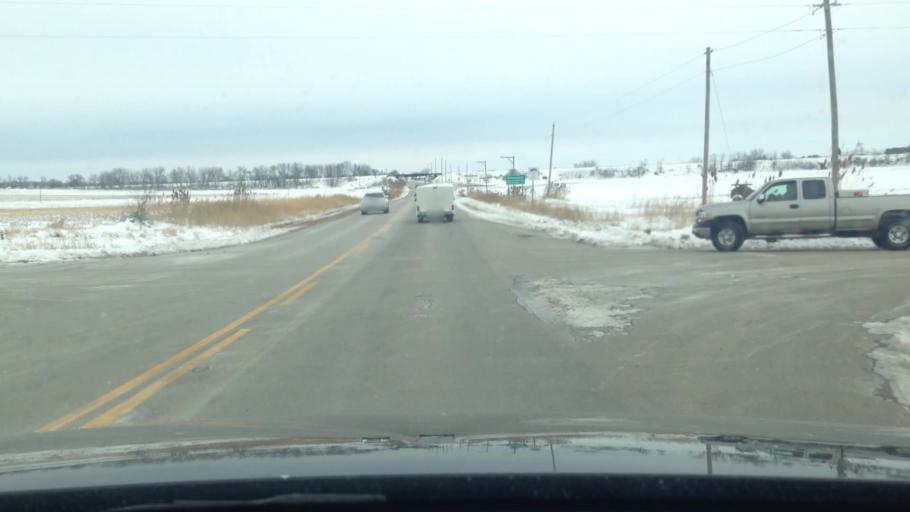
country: US
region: Illinois
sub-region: McHenry County
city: Hebron
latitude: 42.4945
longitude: -88.4423
